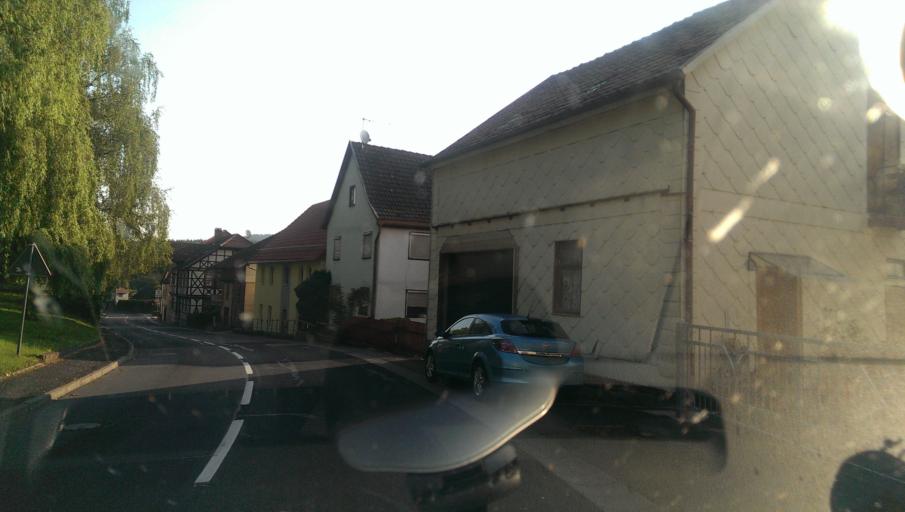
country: DE
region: Thuringia
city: Wolfershausen
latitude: 50.4702
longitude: 10.4406
